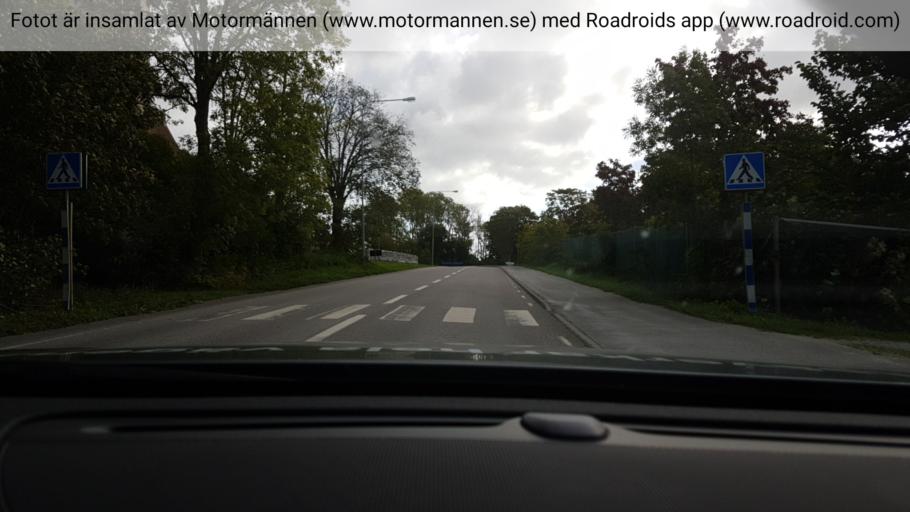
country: SE
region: Gotland
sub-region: Gotland
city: Slite
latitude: 57.7374
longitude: 18.6223
